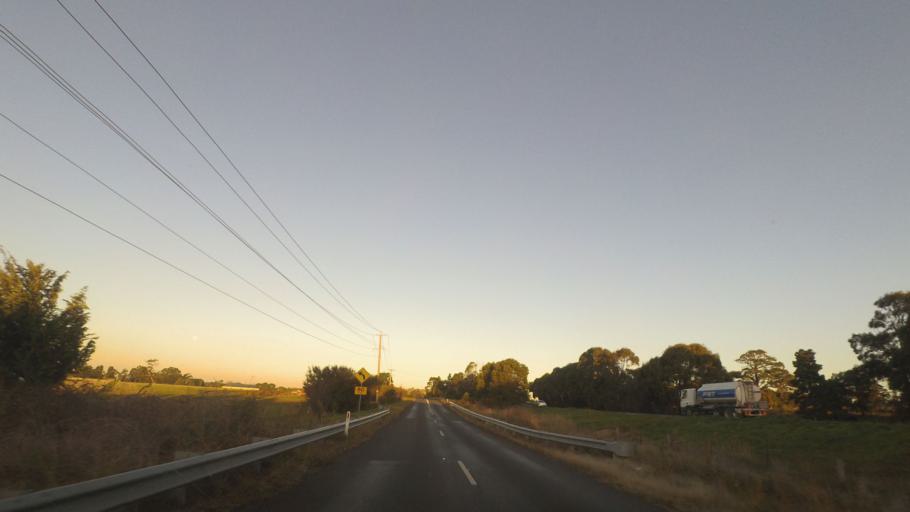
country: AU
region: Victoria
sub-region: Hume
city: Sunbury
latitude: -37.5184
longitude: 144.6238
